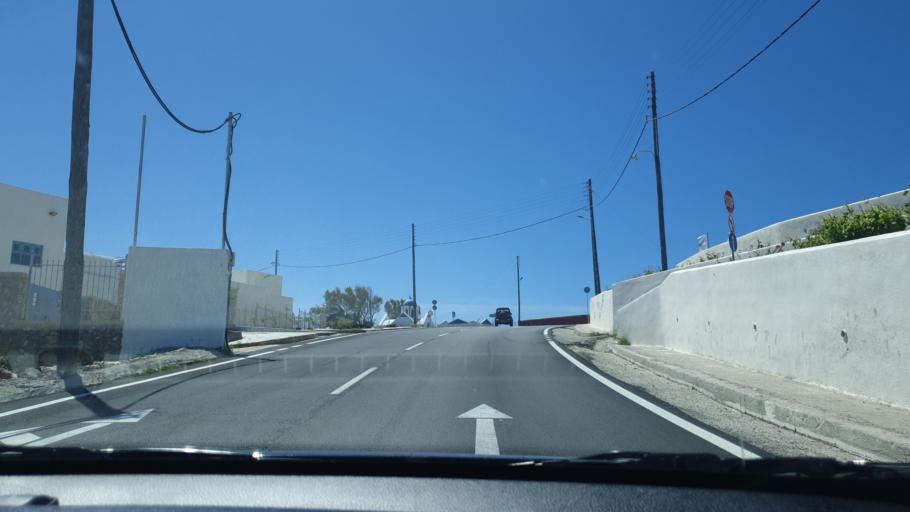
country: GR
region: South Aegean
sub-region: Nomos Kykladon
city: Mesaria
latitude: 36.3877
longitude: 25.4380
